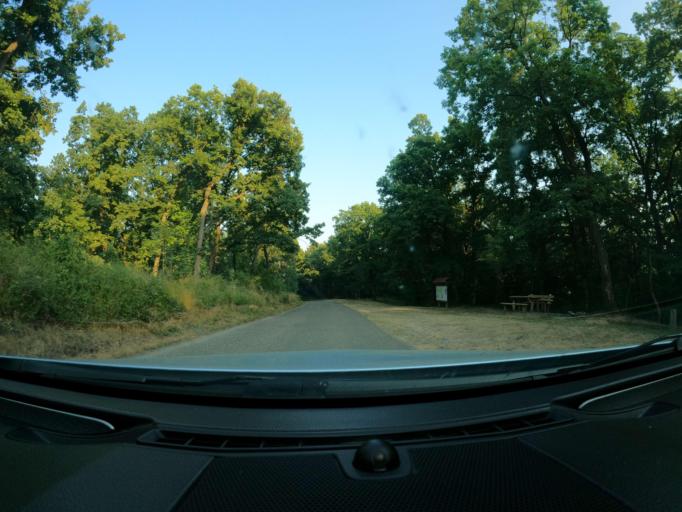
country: RS
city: Vrdnik
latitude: 45.1603
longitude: 19.7696
